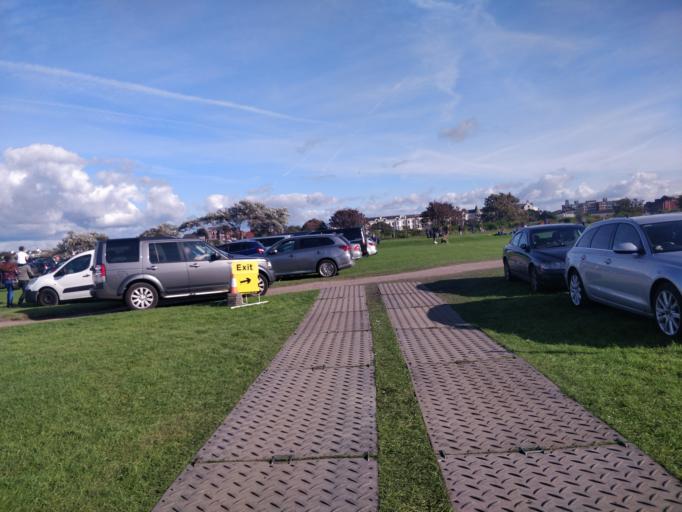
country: GB
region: England
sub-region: Sefton
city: Southport
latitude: 53.6499
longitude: -3.0150
